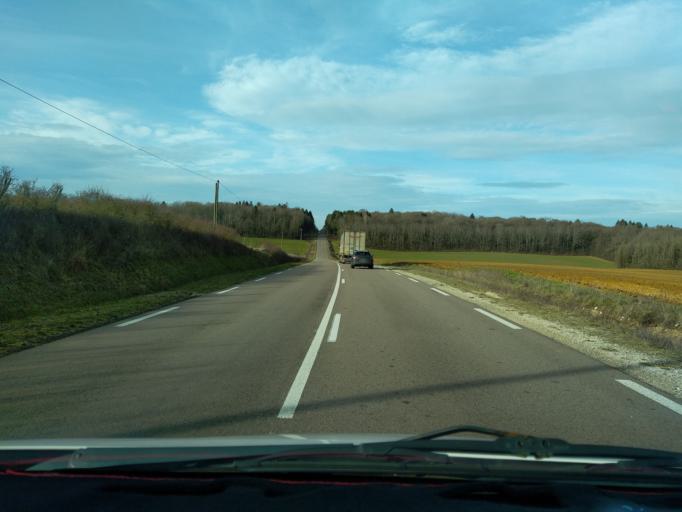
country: FR
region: Franche-Comte
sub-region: Departement de la Haute-Saone
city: Gray
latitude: 47.3967
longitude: 5.6486
